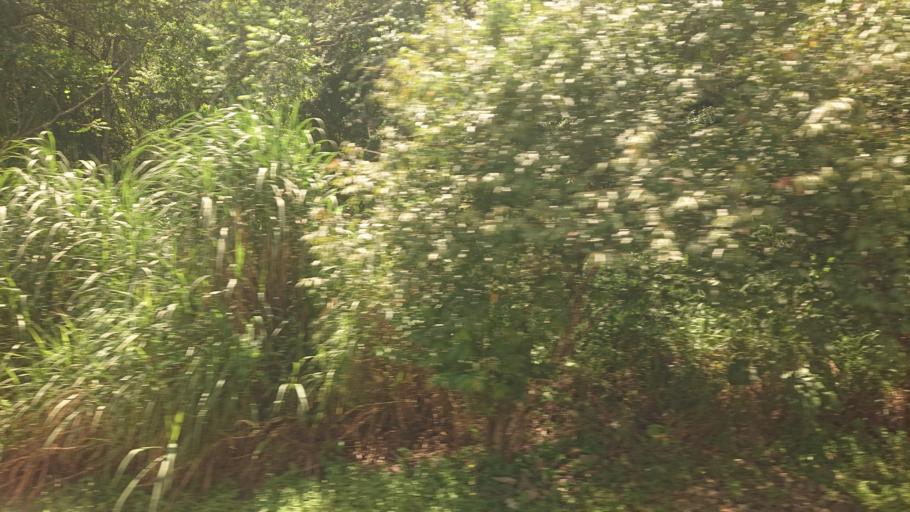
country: TW
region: Taiwan
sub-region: Nantou
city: Puli
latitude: 24.0575
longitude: 120.9349
